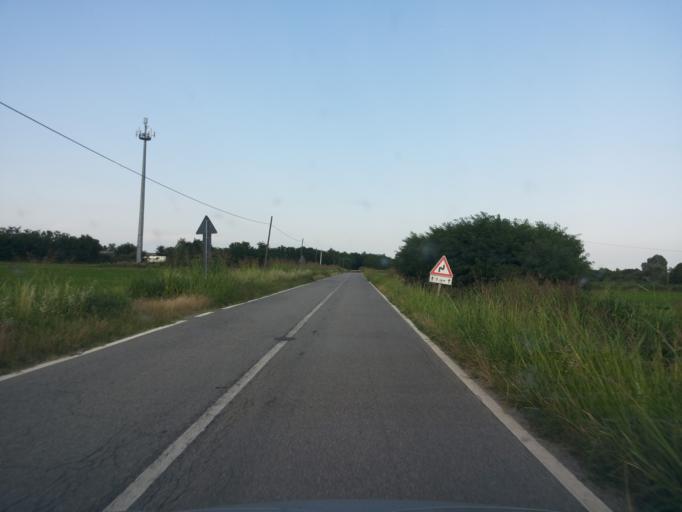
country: IT
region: Piedmont
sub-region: Provincia di Vercelli
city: Asigliano Vercellese
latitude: 45.2646
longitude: 8.4227
